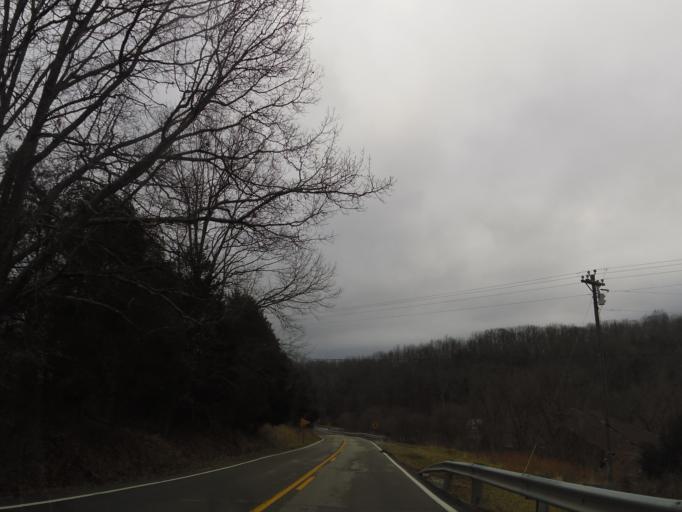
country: US
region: Kentucky
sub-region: Franklin County
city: Frankfort
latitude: 38.3231
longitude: -84.9508
